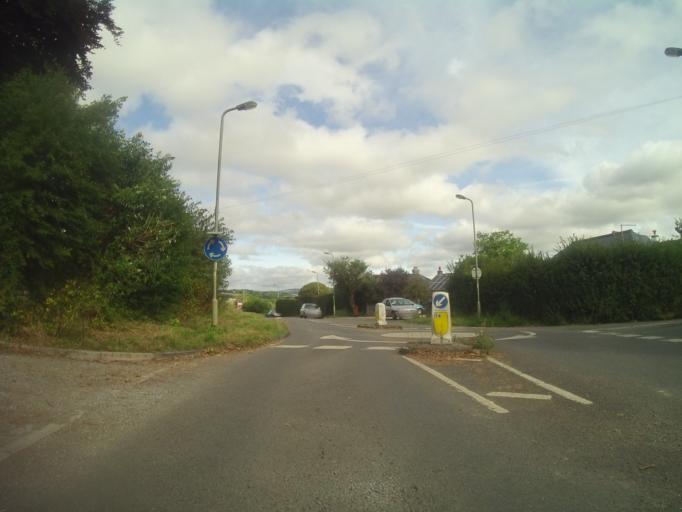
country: GB
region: England
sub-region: Devon
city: Totnes
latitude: 50.4406
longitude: -3.7062
